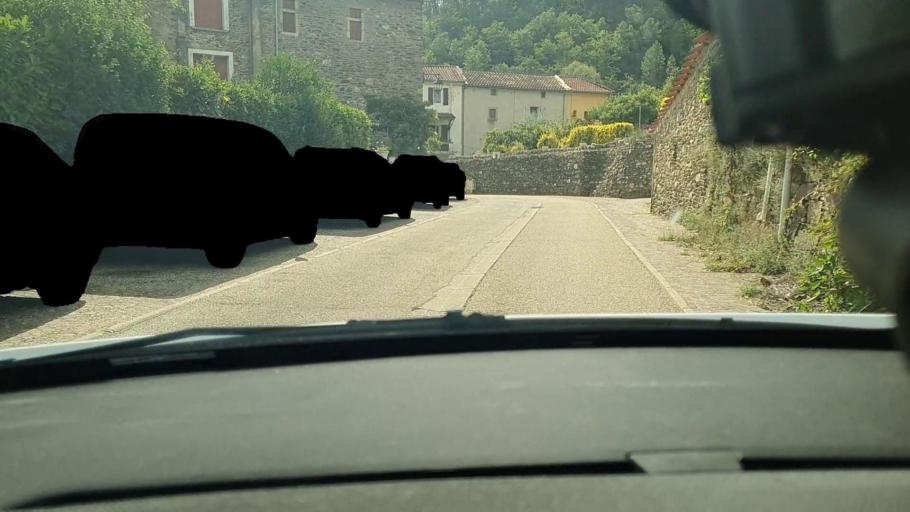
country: FR
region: Languedoc-Roussillon
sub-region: Departement du Gard
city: Besseges
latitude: 44.3040
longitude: 4.0597
